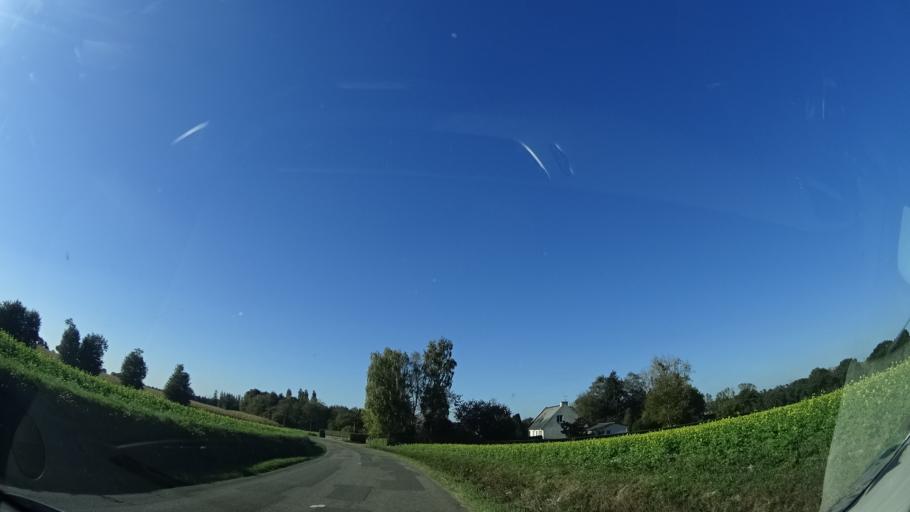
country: FR
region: Brittany
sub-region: Departement d'Ille-et-Vilaine
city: La Meziere
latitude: 48.2239
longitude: -1.7646
